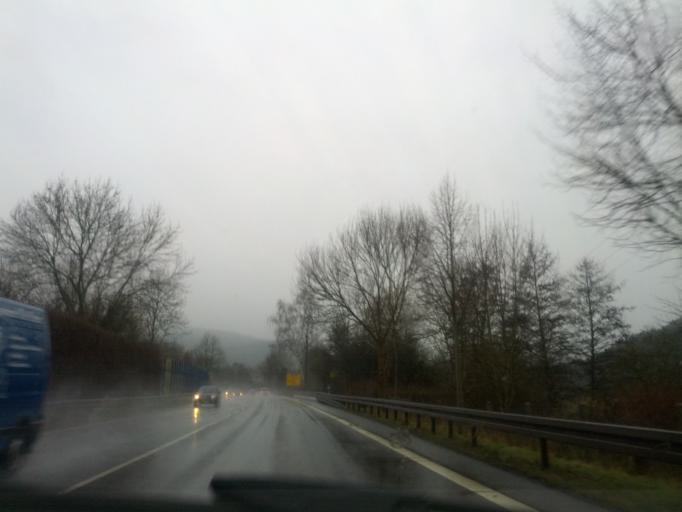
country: DE
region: Hesse
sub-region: Regierungsbezirk Kassel
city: Sontra
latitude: 51.1090
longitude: 9.9679
